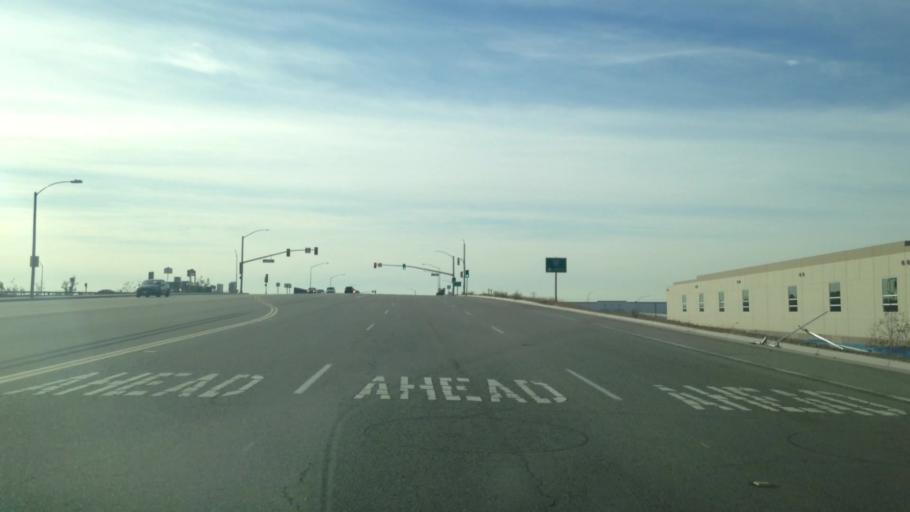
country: US
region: California
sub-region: Riverside County
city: Mira Loma
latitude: 34.0034
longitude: -117.5470
